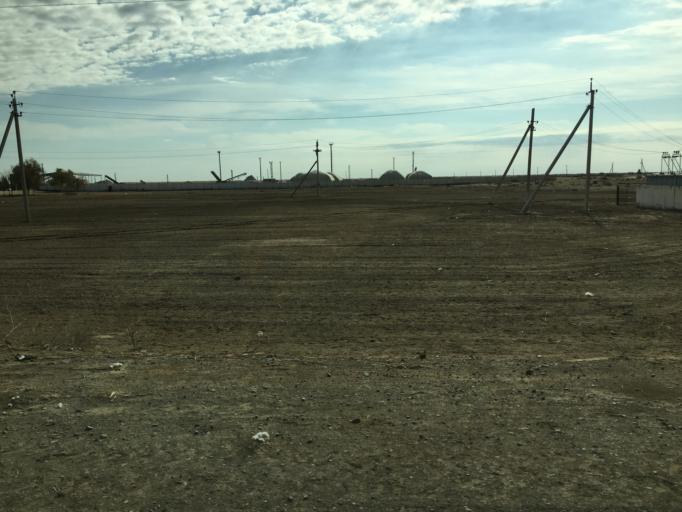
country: TM
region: Ahal
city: Tejen
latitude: 37.4464
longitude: 61.1304
